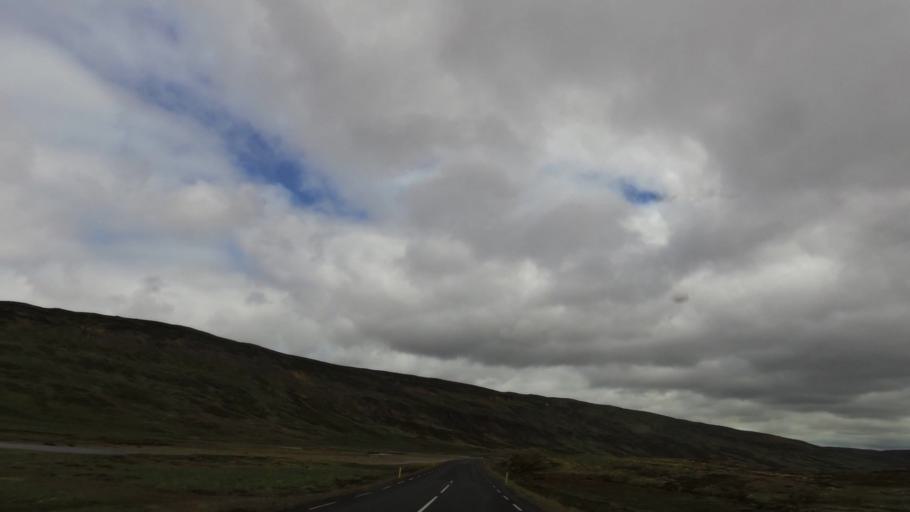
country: IS
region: West
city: Stykkisholmur
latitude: 65.7620
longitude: -21.8409
